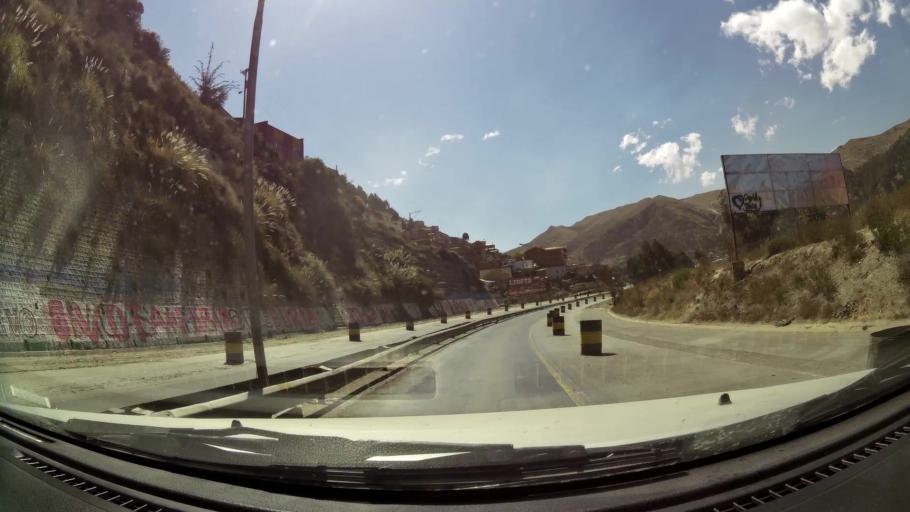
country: BO
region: La Paz
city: La Paz
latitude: -16.4637
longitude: -68.1535
